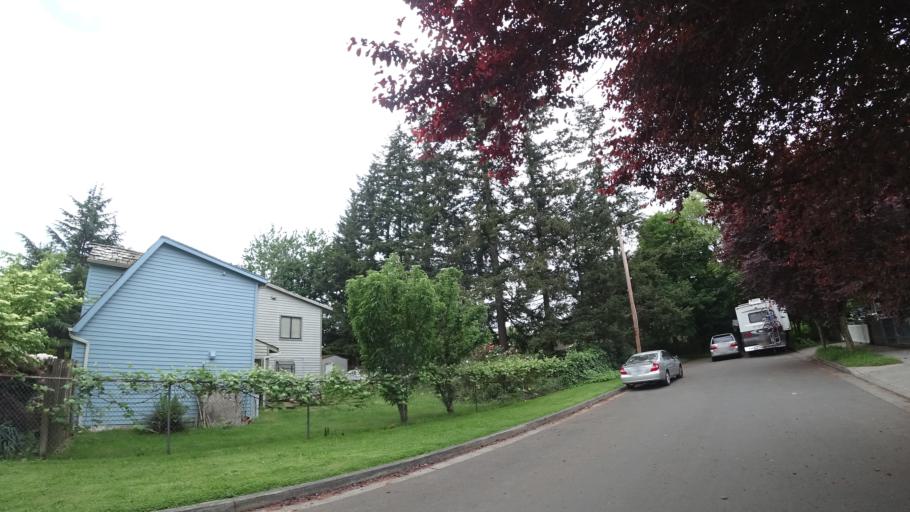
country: US
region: Oregon
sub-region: Multnomah County
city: Gresham
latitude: 45.5083
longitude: -122.4881
